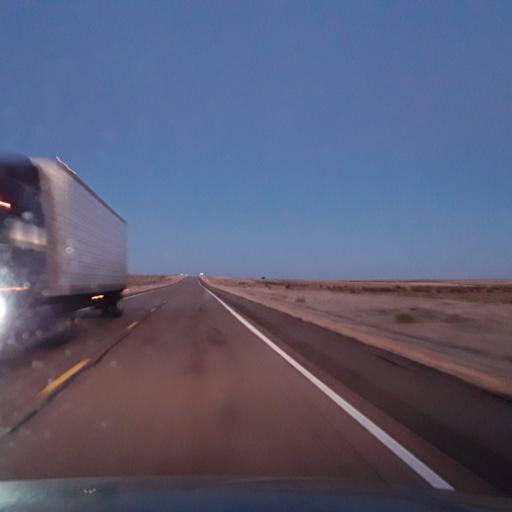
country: US
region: New Mexico
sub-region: Guadalupe County
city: Santa Rosa
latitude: 34.7656
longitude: -104.9776
